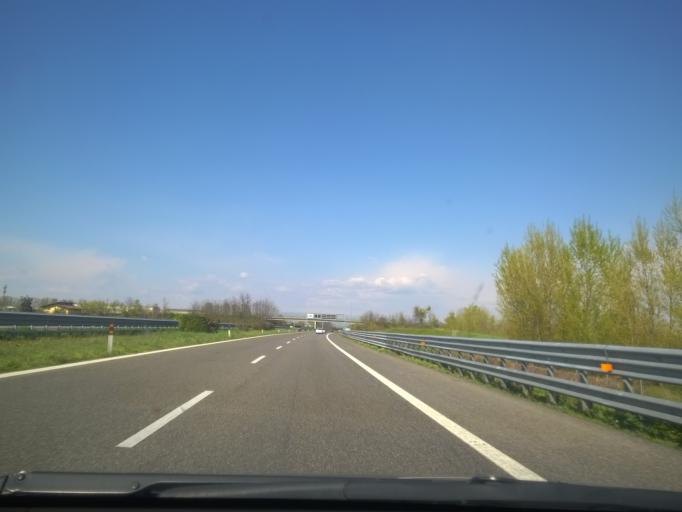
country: IT
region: Lombardy
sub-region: Provincia di Brescia
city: San Gervasio Bresciano
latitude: 45.3055
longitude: 10.1401
